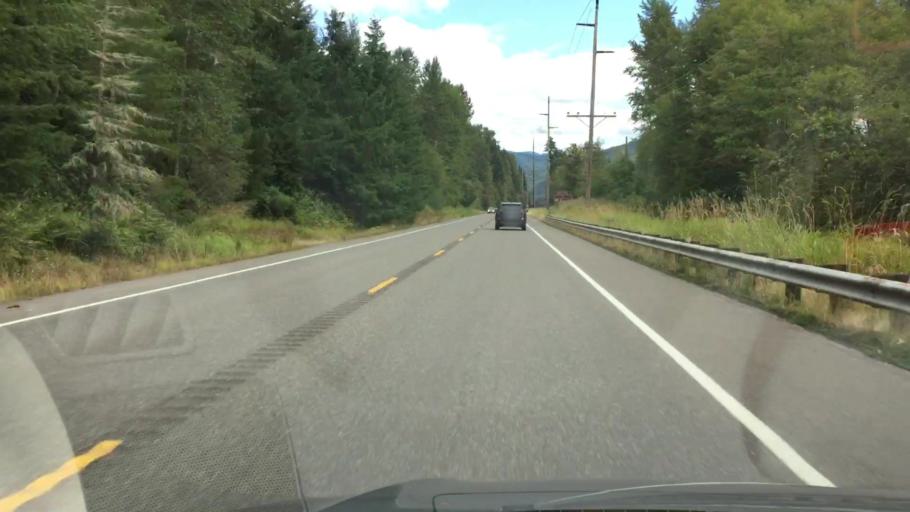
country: US
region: Washington
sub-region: Pierce County
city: Eatonville
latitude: 46.7757
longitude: -122.2222
